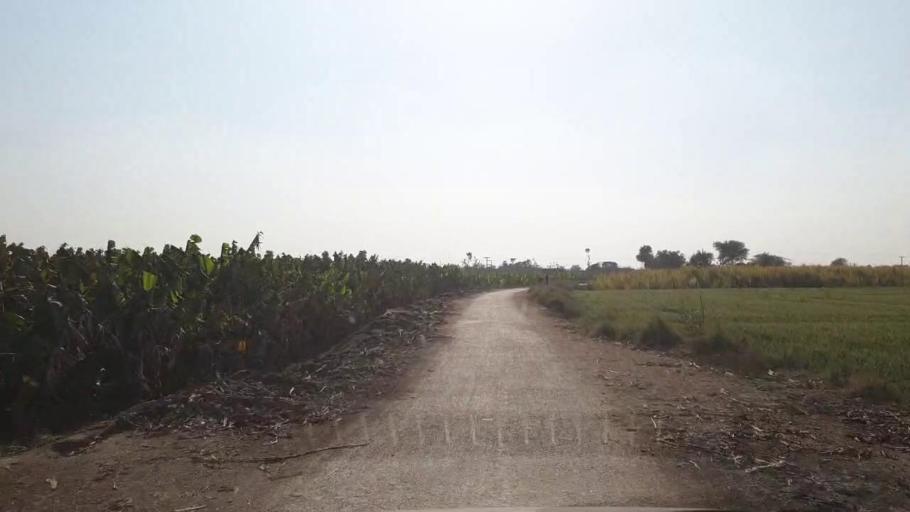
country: PK
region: Sindh
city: Chambar
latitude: 25.3387
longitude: 68.7514
